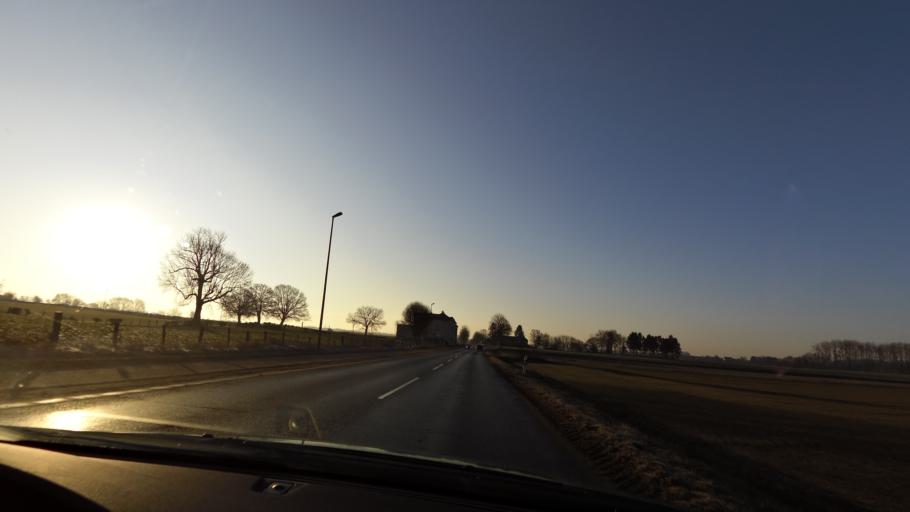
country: NL
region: Limburg
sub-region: Gemeente Kerkrade
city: Kerkrade
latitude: 50.8284
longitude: 6.0504
